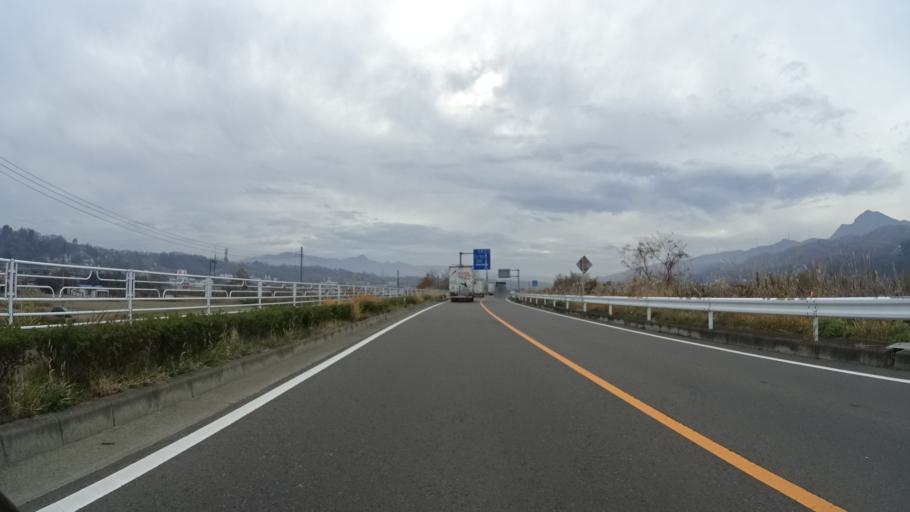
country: JP
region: Gunma
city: Numata
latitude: 36.6477
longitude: 139.0271
